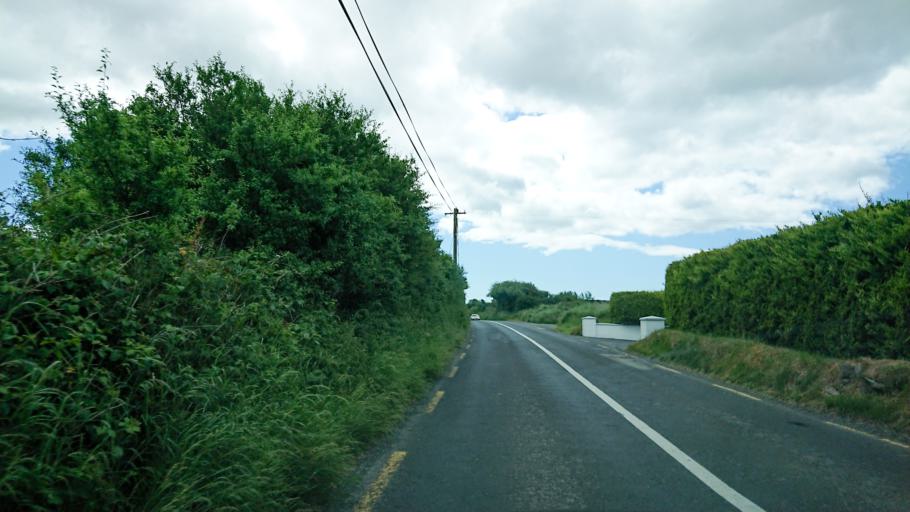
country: IE
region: Munster
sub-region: Waterford
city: Tra Mhor
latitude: 52.1856
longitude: -7.1770
